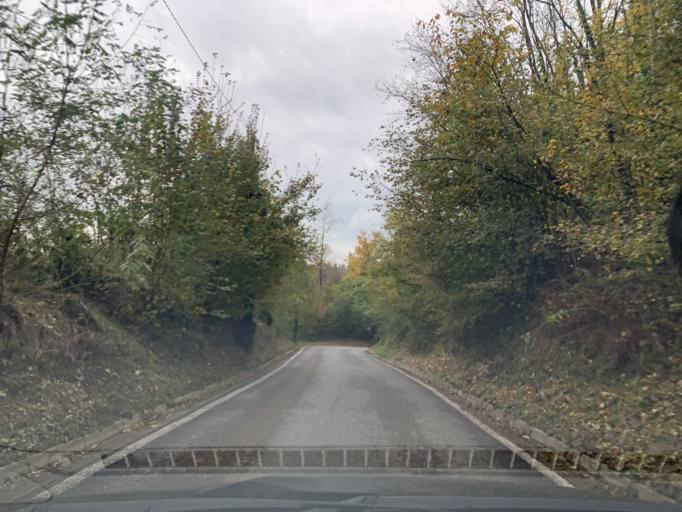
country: IT
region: Lombardy
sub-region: Provincia di Como
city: Casnate Con Bernate
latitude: 45.7456
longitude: 9.0697
